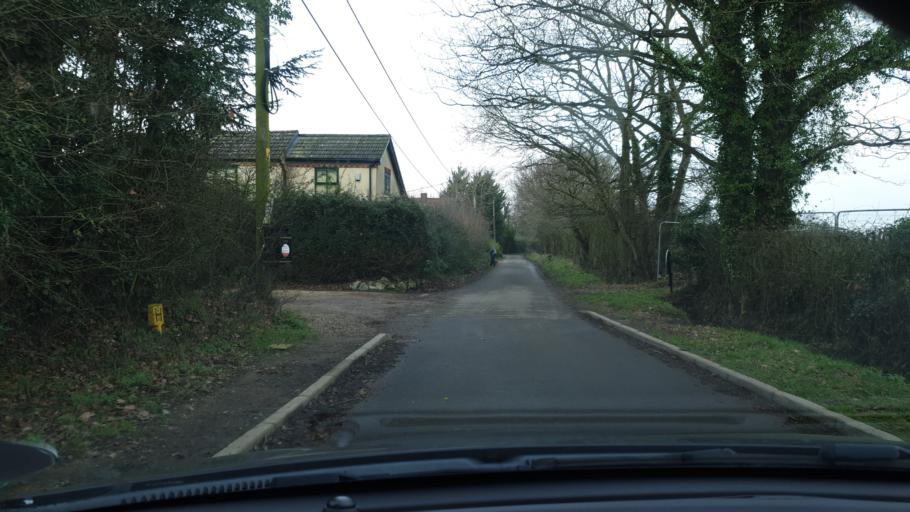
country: GB
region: England
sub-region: Essex
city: Alresford
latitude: 51.8566
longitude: 0.9951
